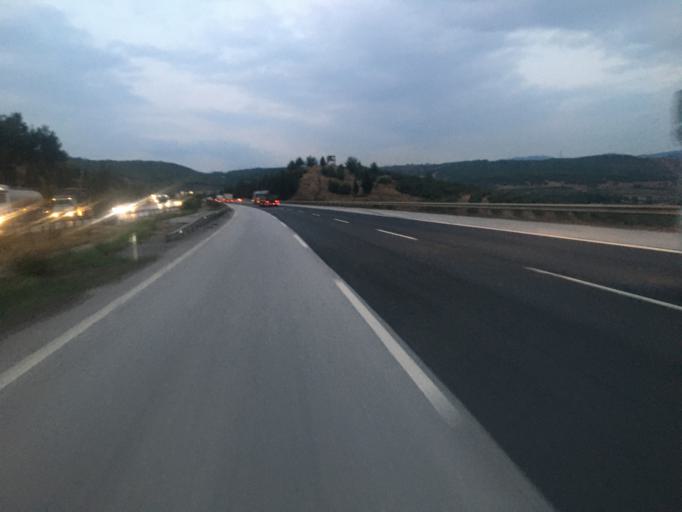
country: TR
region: Osmaniye
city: Kaypak
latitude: 37.1623
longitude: 36.3597
